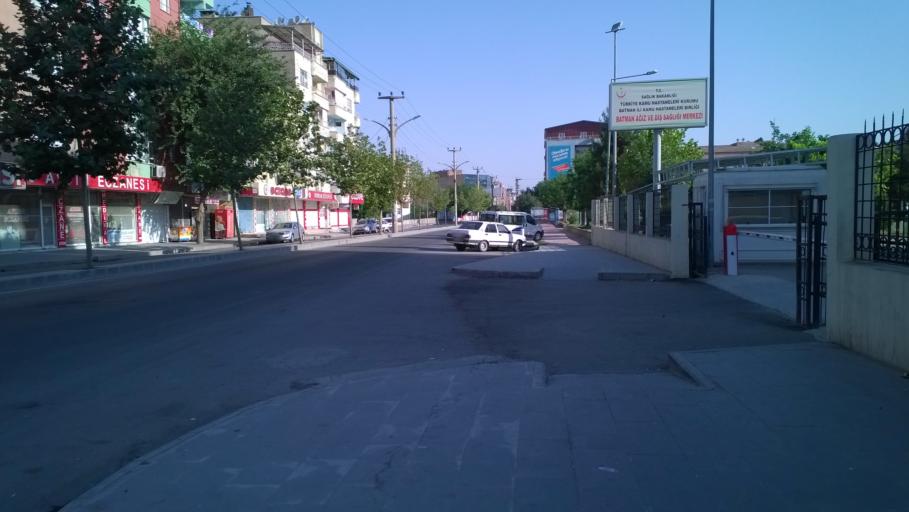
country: TR
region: Batman
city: Batman
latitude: 37.8883
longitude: 41.1256
